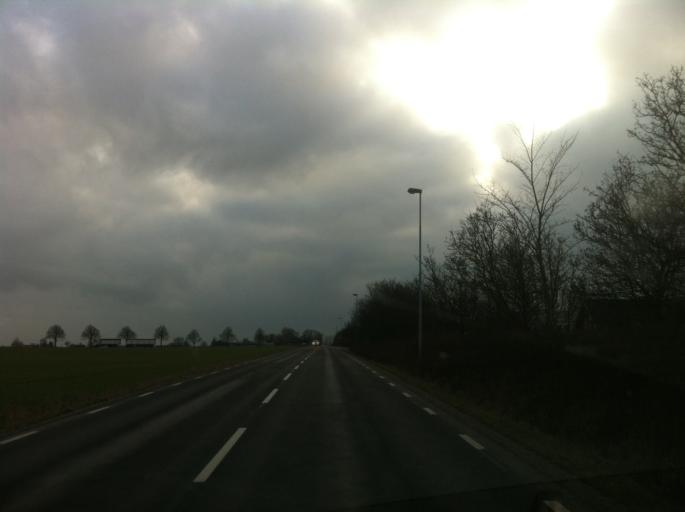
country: SE
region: Skane
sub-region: Landskrona
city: Asmundtorp
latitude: 55.8780
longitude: 12.9978
